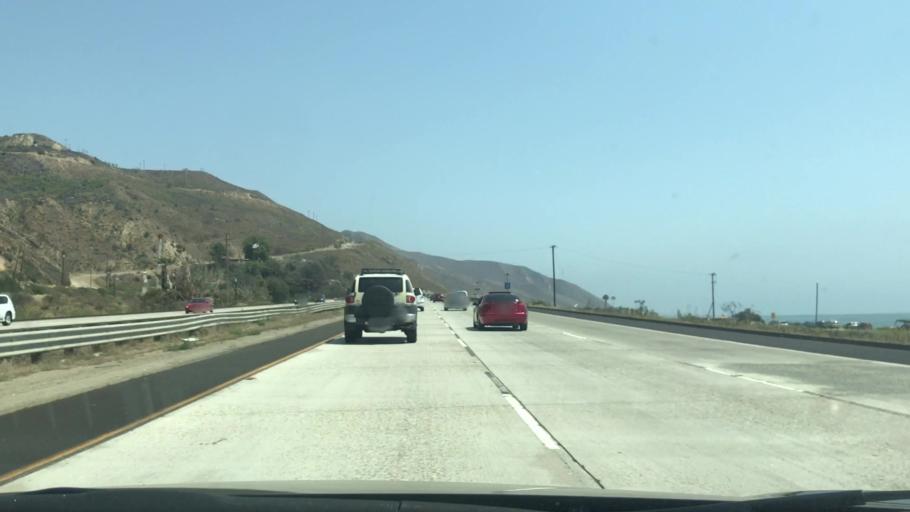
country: US
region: California
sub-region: Ventura County
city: Ventura
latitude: 34.3197
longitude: -119.3684
